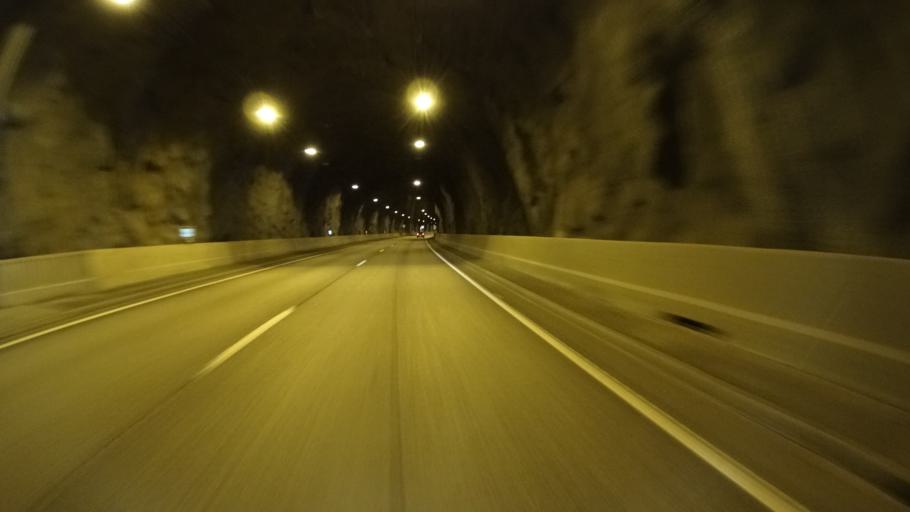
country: FI
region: Uusimaa
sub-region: Helsinki
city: Vantaa
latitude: 60.2282
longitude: 25.1647
